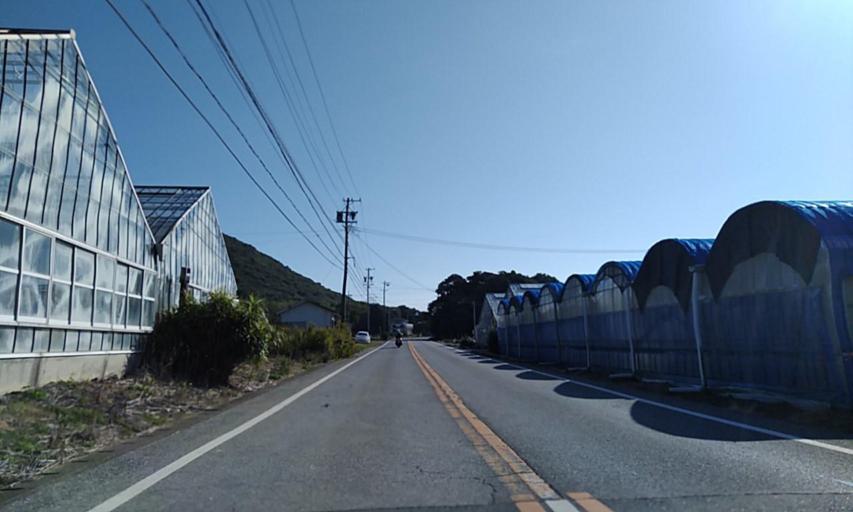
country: JP
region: Aichi
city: Tahara
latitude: 34.5920
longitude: 137.1000
